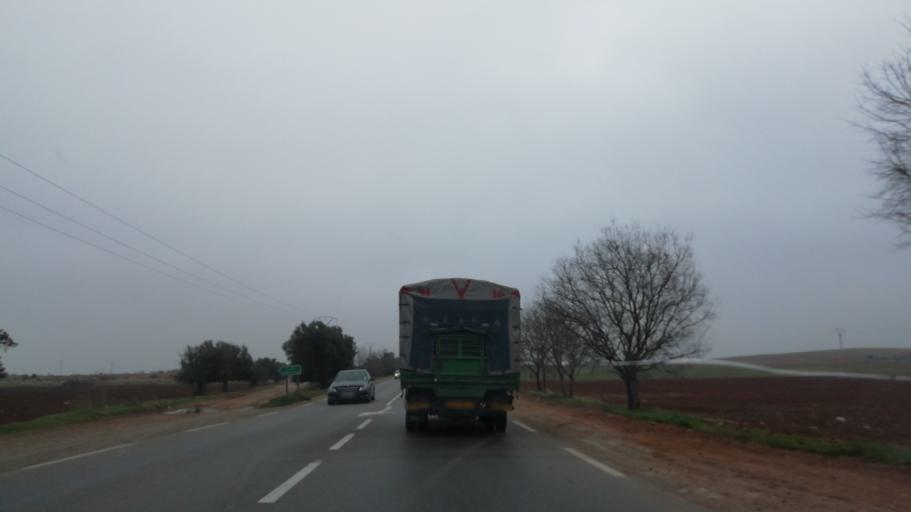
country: DZ
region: Mascara
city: Mascara
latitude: 35.3179
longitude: 0.3712
